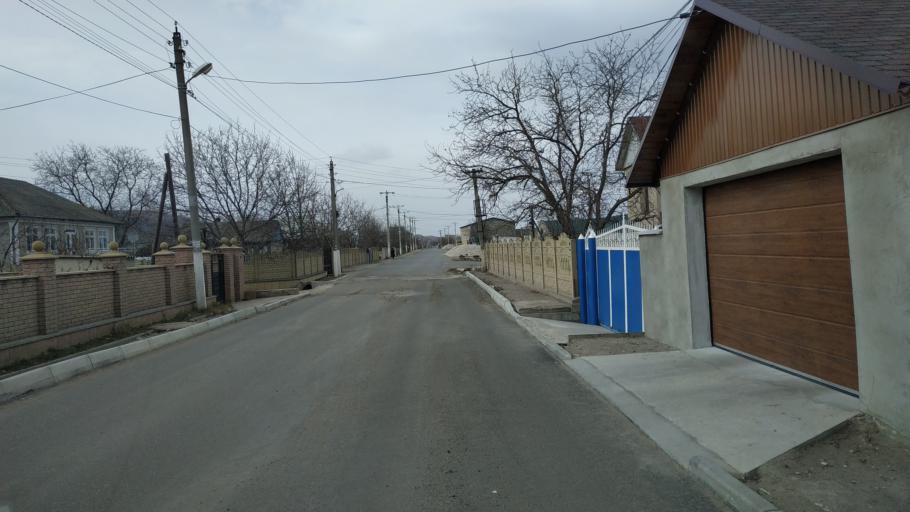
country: MD
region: Laloveni
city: Ialoveni
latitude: 46.8608
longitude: 28.7837
